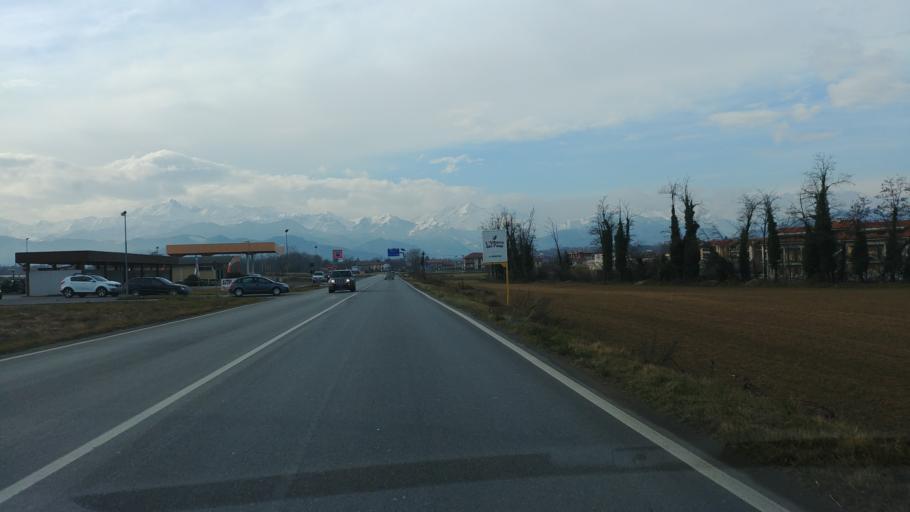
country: IT
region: Piedmont
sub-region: Provincia di Cuneo
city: Cuneo
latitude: 44.3880
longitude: 7.5704
